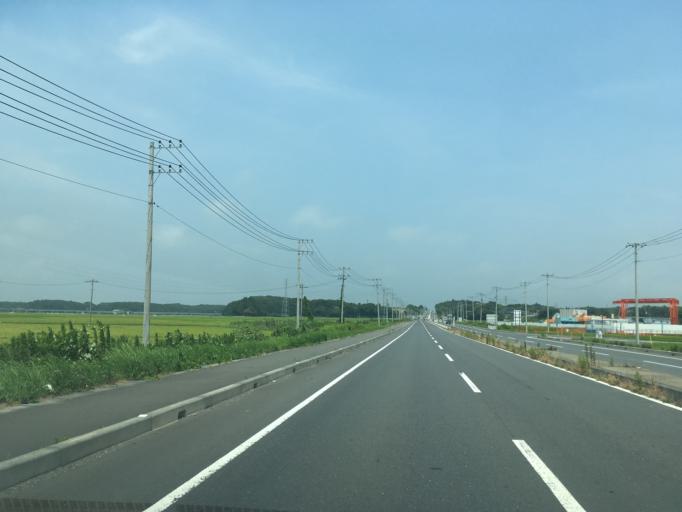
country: JP
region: Ibaraki
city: Oarai
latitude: 36.3559
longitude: 140.5798
